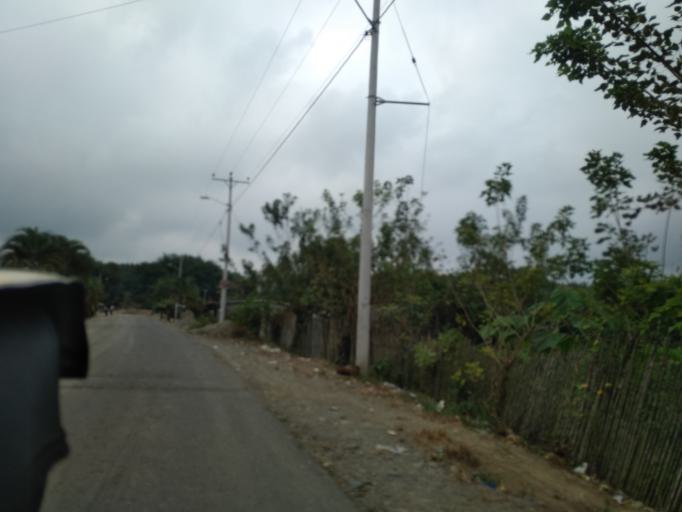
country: EC
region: Los Rios
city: Quevedo
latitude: -0.9795
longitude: -79.3530
